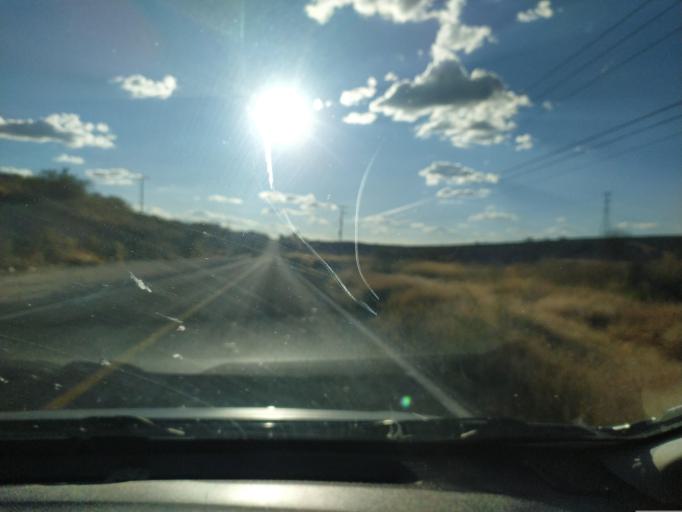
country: MX
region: Guanajuato
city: San Francisco del Rincon
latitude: 21.0368
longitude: -101.9120
